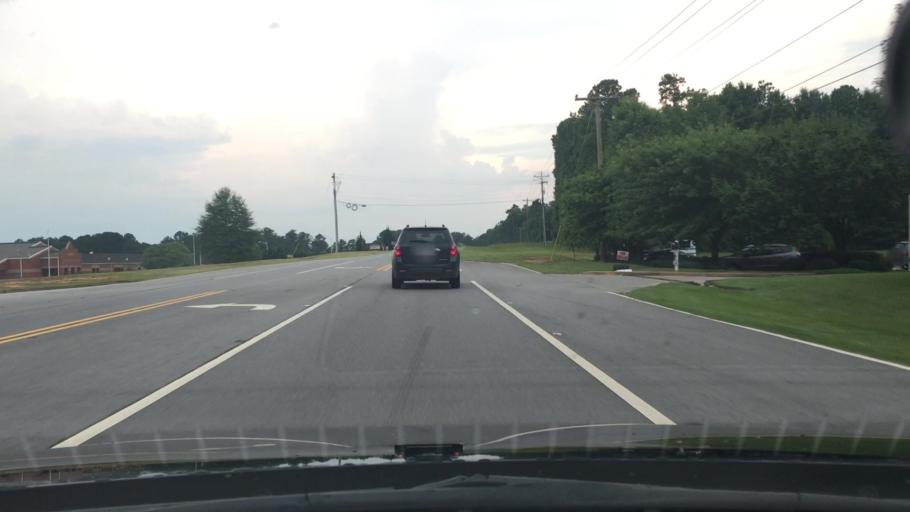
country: US
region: Georgia
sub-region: Coweta County
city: East Newnan
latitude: 33.3424
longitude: -84.6878
